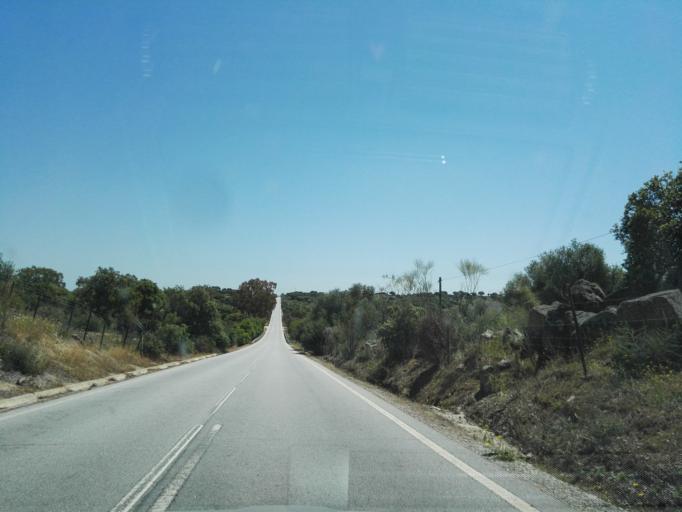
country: PT
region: Portalegre
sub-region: Elvas
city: Elvas
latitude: 39.0011
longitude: -7.2109
